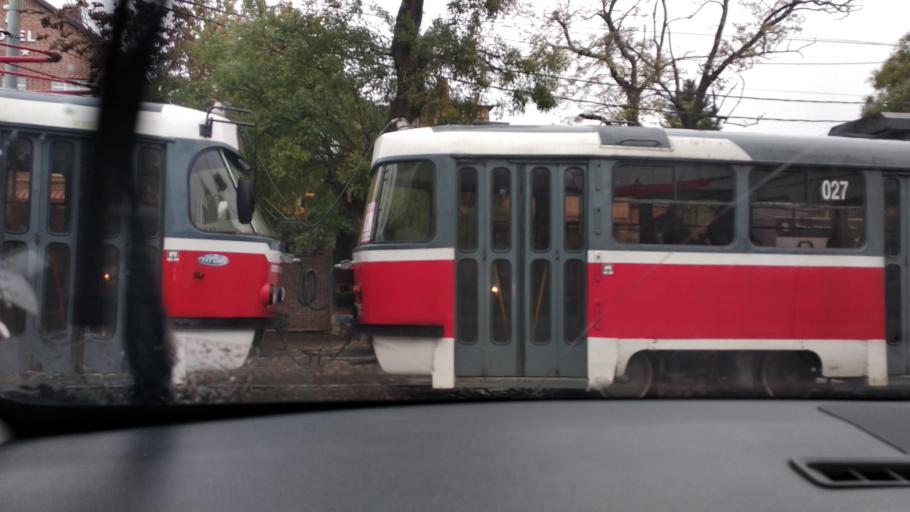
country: RU
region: Krasnodarskiy
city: Krasnodar
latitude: 45.0284
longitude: 38.9897
